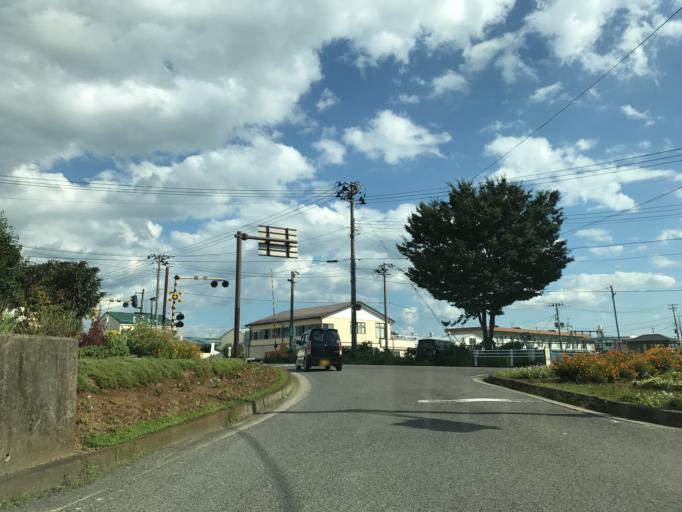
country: JP
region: Fukushima
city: Koriyama
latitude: 37.4099
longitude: 140.3933
